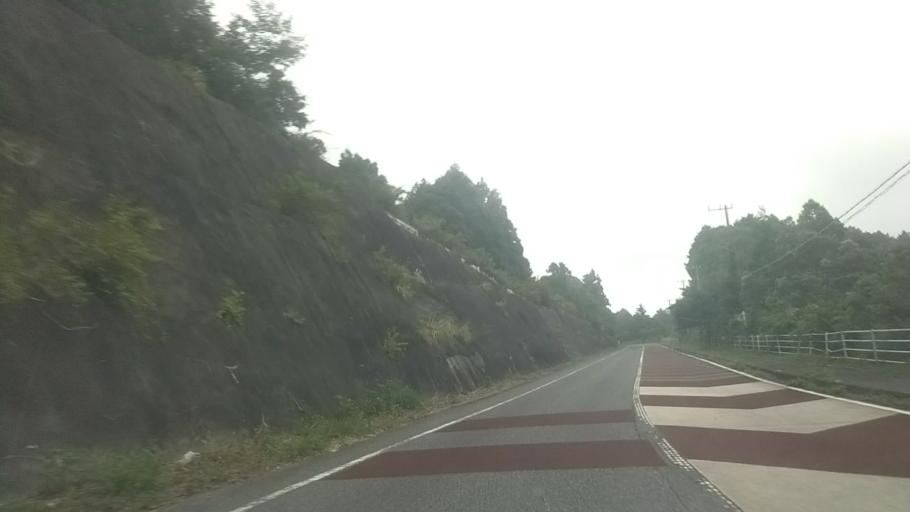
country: JP
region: Chiba
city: Kawaguchi
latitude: 35.1511
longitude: 140.1471
